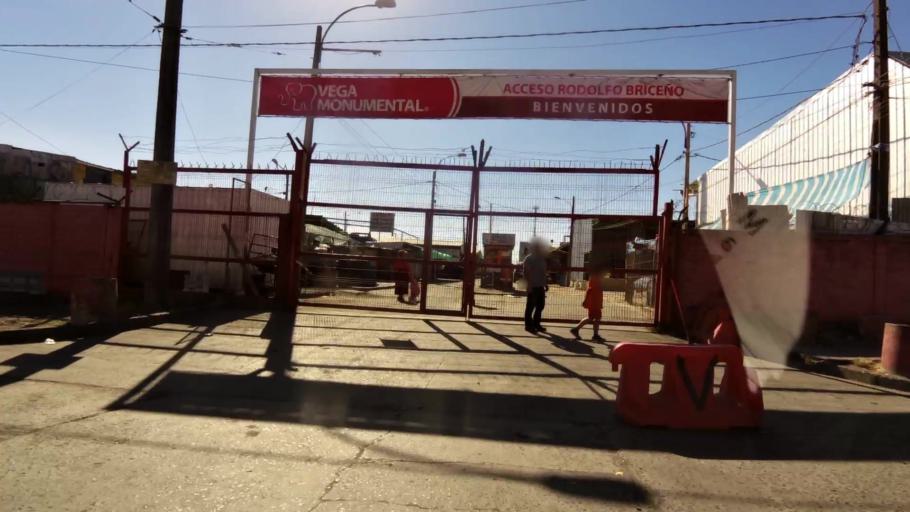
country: CL
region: Biobio
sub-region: Provincia de Concepcion
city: Concepcion
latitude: -36.8121
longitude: -73.0783
